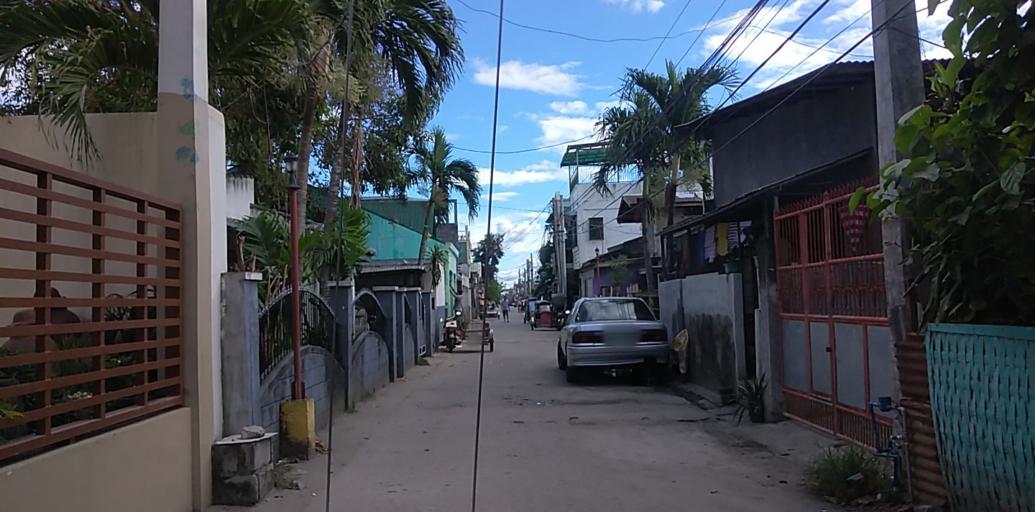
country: PH
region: Central Luzon
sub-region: Province of Pampanga
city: Arayat
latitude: 15.1431
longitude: 120.7683
